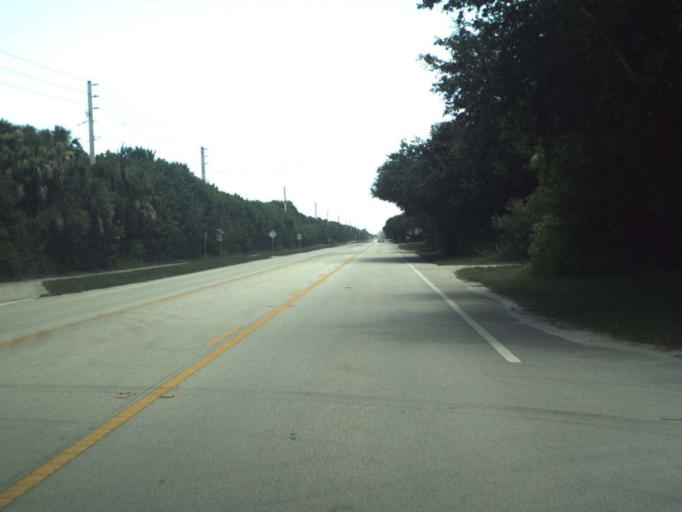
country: US
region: Florida
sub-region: Indian River County
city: Wabasso Beach
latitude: 27.7677
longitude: -80.4006
